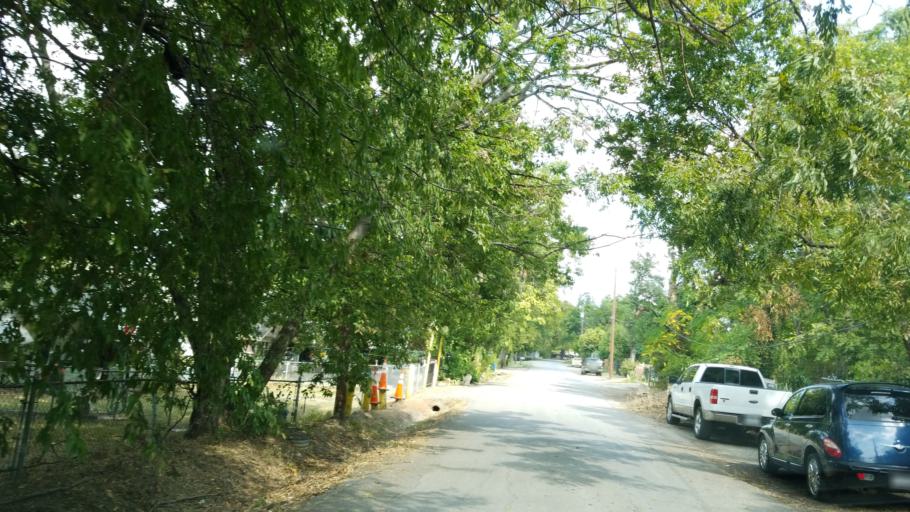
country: US
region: Texas
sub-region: Dallas County
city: Dallas
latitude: 32.7717
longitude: -96.8503
